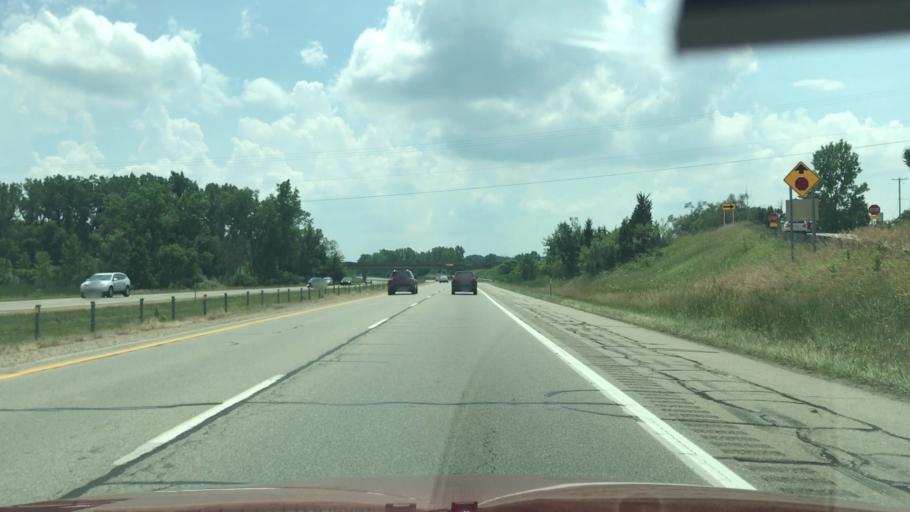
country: US
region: Michigan
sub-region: Allegan County
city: Wayland
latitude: 42.5970
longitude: -85.6622
